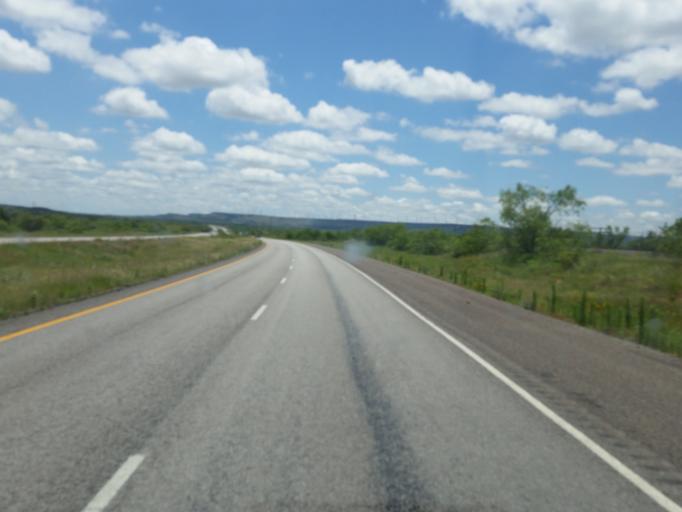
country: US
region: Texas
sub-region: Garza County
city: Post
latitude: 33.0145
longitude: -101.1767
